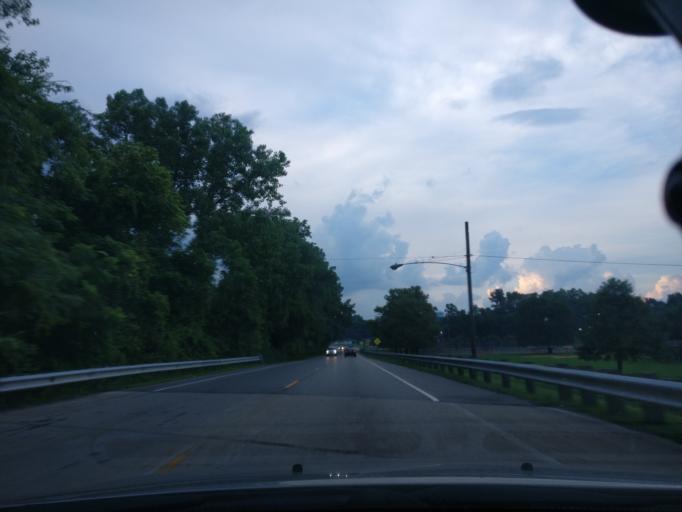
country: US
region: Ohio
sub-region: Warren County
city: Franklin
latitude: 39.5515
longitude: -84.2984
